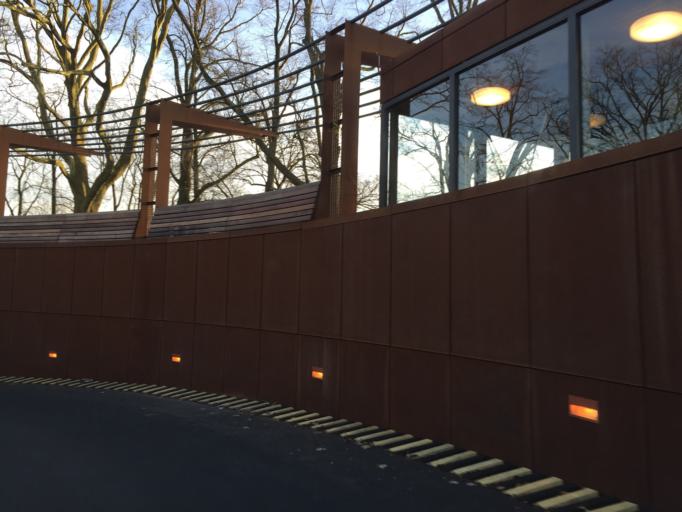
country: NL
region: North Brabant
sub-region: Gemeente 's-Hertogenbosch
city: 's-Hertogenbosch
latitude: 51.6852
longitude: 5.3141
